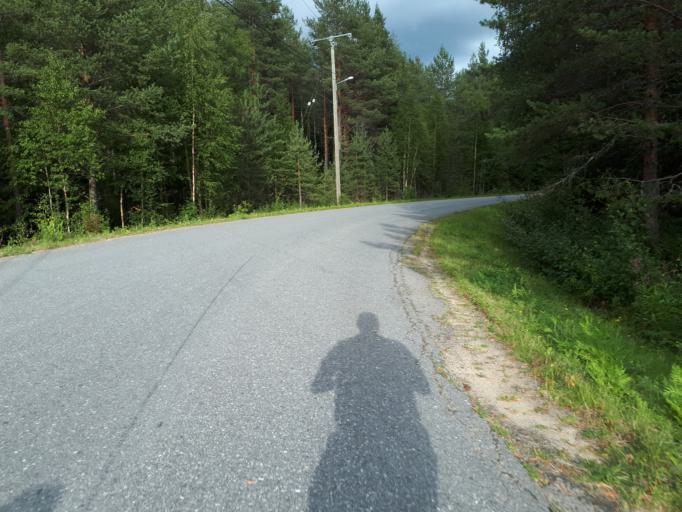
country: FI
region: Northern Ostrobothnia
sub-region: Oulunkaari
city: Ii
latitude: 65.3329
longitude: 25.3871
